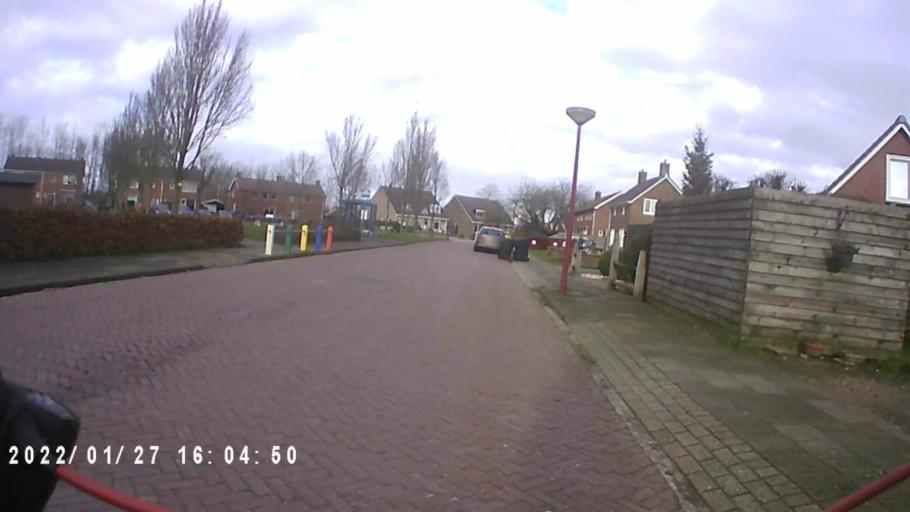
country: NL
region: Friesland
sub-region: Gemeente Dongeradeel
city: Anjum
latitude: 53.3811
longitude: 6.0888
